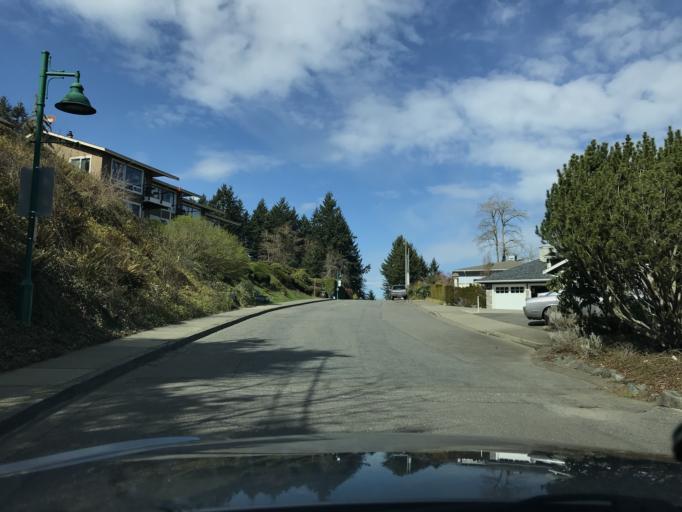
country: US
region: Washington
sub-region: Pierce County
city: Gig Harbor
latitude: 47.3259
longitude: -122.5768
